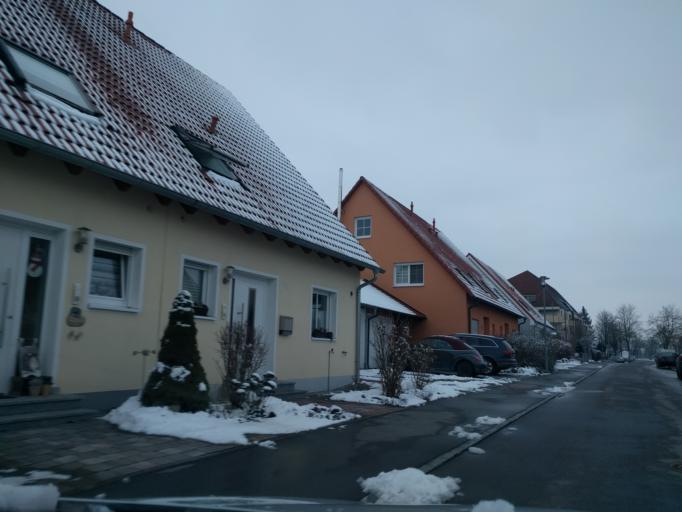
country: DE
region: Bavaria
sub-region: Swabia
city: Donauwoerth
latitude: 48.7168
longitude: 10.7544
